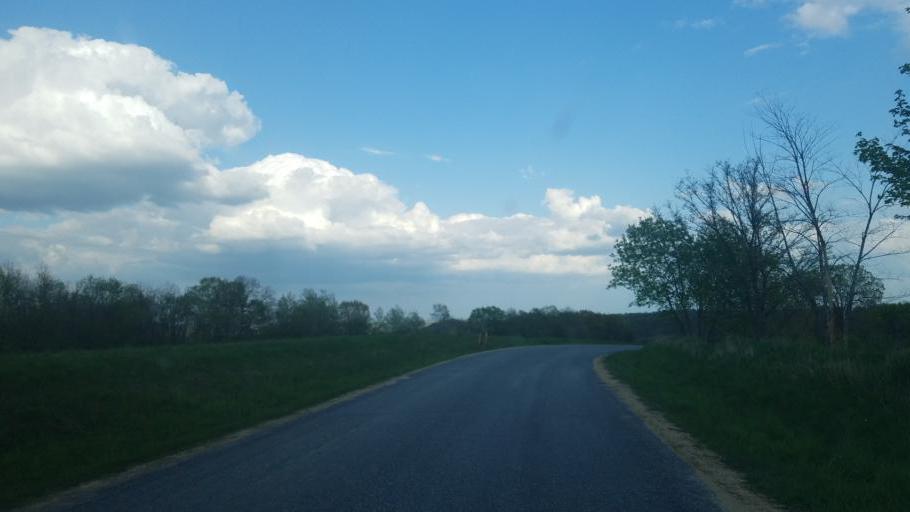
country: US
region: Wisconsin
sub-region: Vernon County
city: Hillsboro
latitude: 43.6836
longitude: -90.3759
